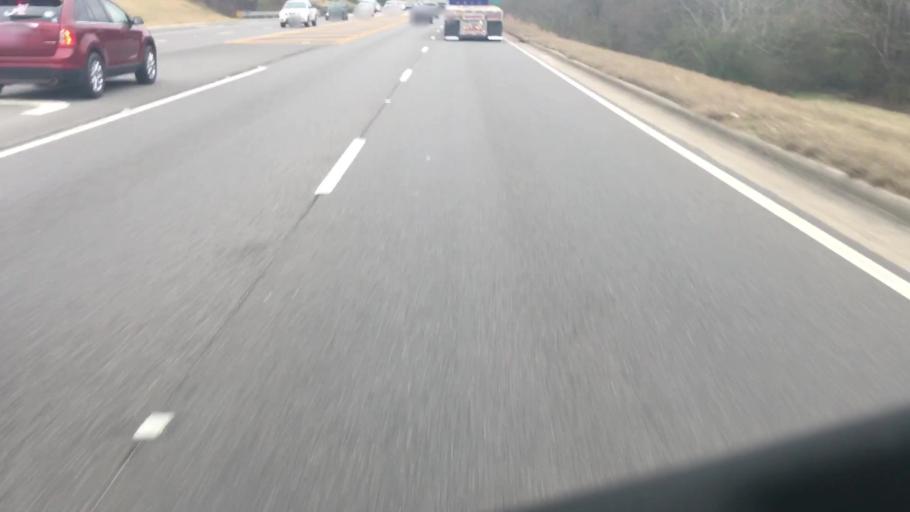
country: US
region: Alabama
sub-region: Jefferson County
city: Hoover
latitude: 33.3659
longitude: -86.8228
